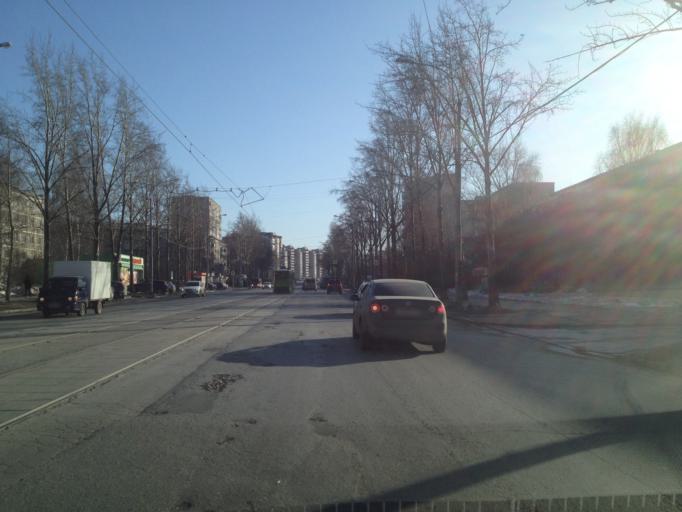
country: RU
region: Sverdlovsk
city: Sovkhoznyy
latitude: 56.8299
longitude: 60.5445
